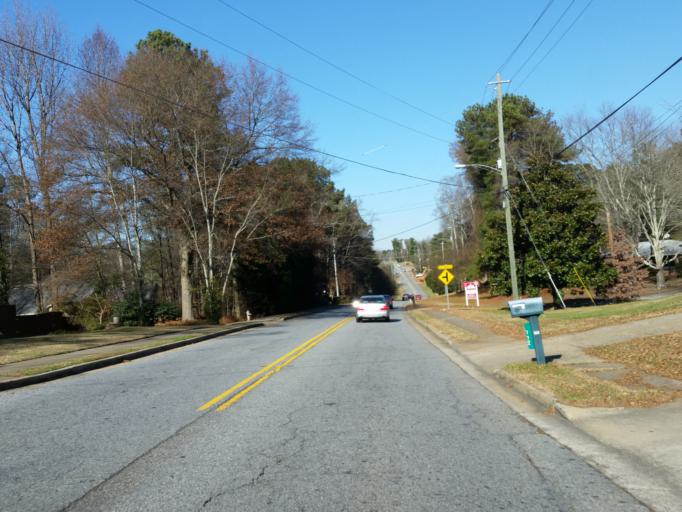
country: US
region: Georgia
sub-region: Cobb County
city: Marietta
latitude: 33.9687
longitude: -84.4627
